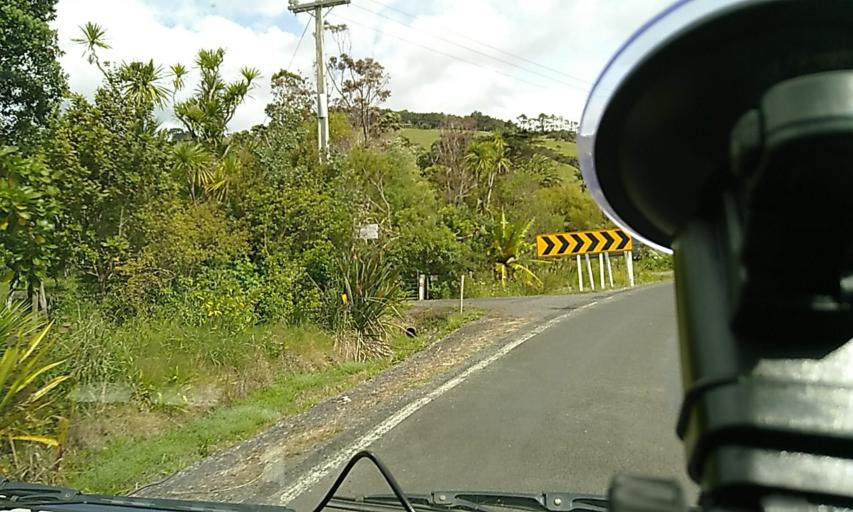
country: NZ
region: Northland
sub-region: Far North District
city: Ahipara
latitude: -35.5311
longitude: 173.3901
